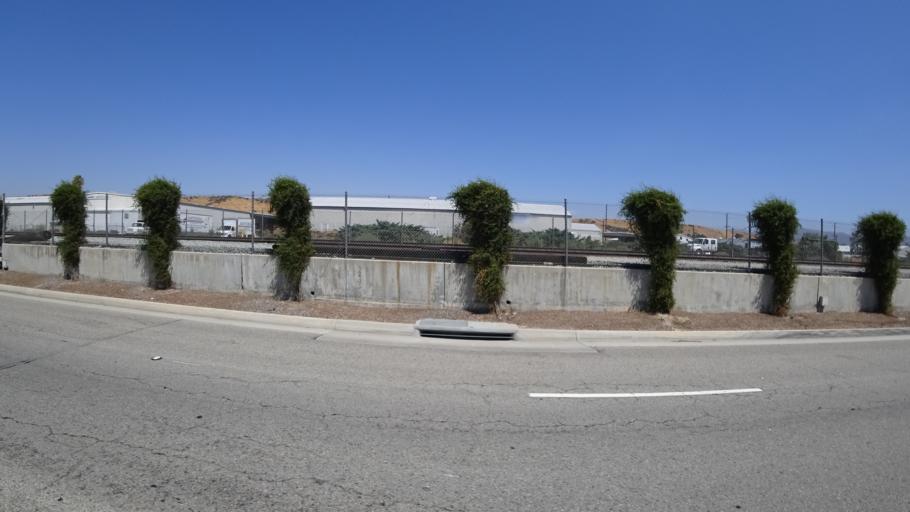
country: US
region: California
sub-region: Los Angeles County
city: Santa Clarita
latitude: 34.4079
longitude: -118.5399
